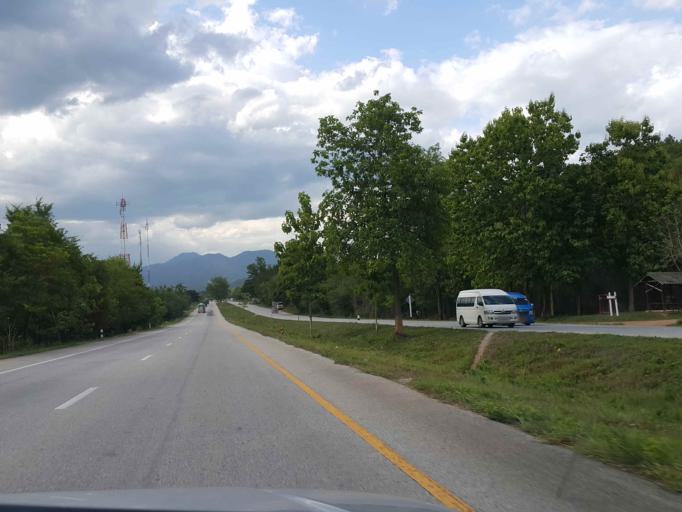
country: TH
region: Lampang
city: Thoen
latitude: 17.7111
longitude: 99.2294
